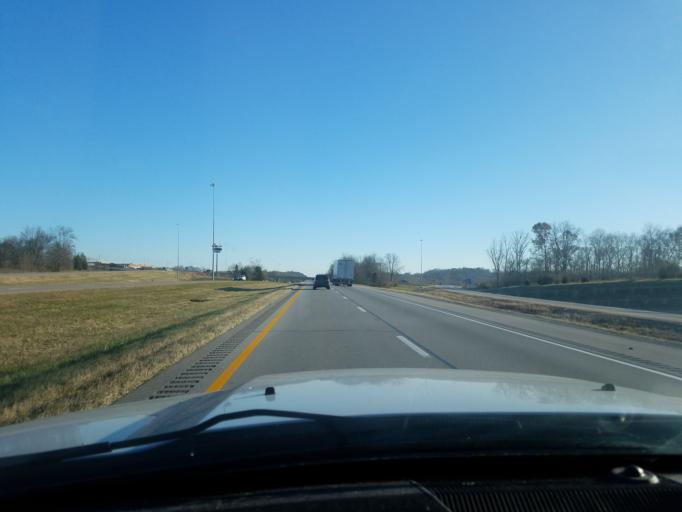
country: US
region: Kentucky
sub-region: Gallatin County
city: Warsaw
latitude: 38.6894
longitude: -84.9438
